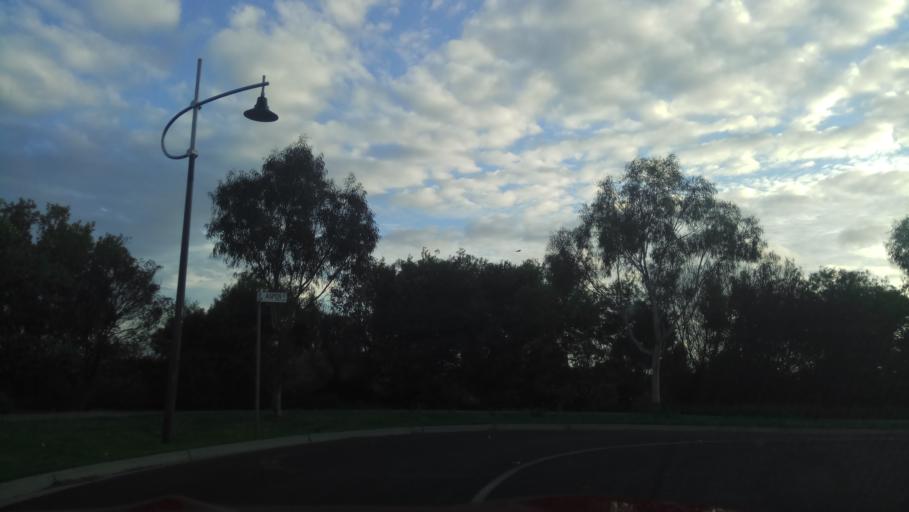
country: AU
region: Victoria
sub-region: Wyndham
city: Point Cook
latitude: -37.9131
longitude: 144.7430
